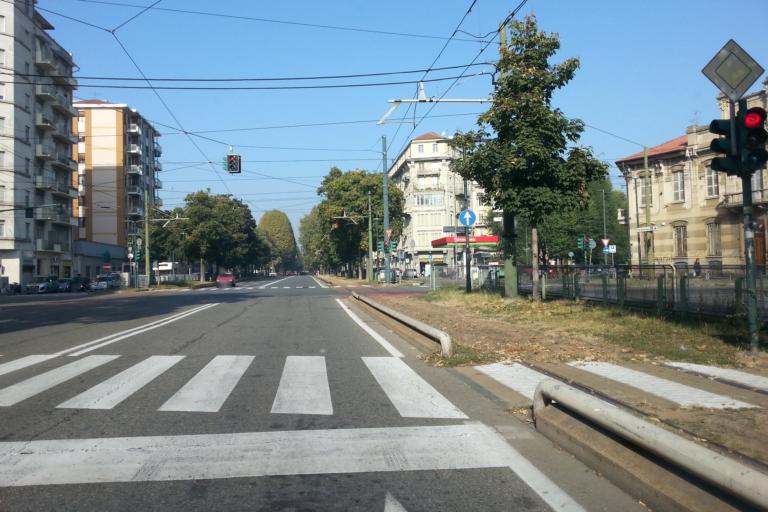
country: IT
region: Piedmont
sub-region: Provincia di Torino
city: Turin
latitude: 45.0698
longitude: 7.7047
